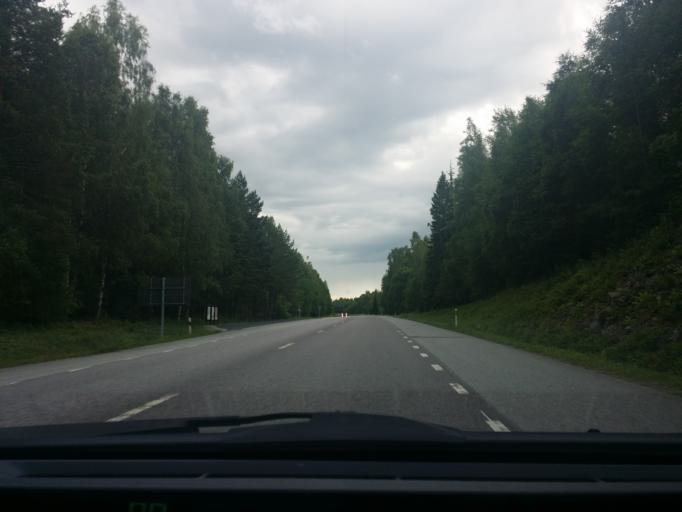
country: SE
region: OErebro
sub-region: Nora Kommun
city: Nora
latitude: 59.5016
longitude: 15.0323
